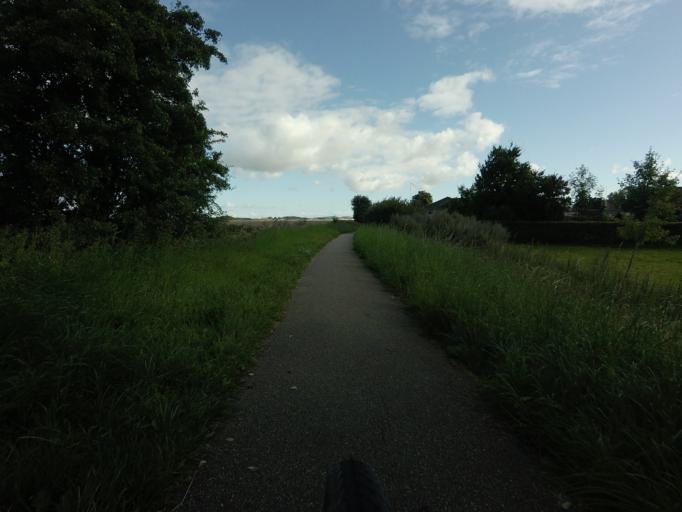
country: DK
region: Central Jutland
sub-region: Horsens Kommune
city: Horsens
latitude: 55.9004
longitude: 9.7581
